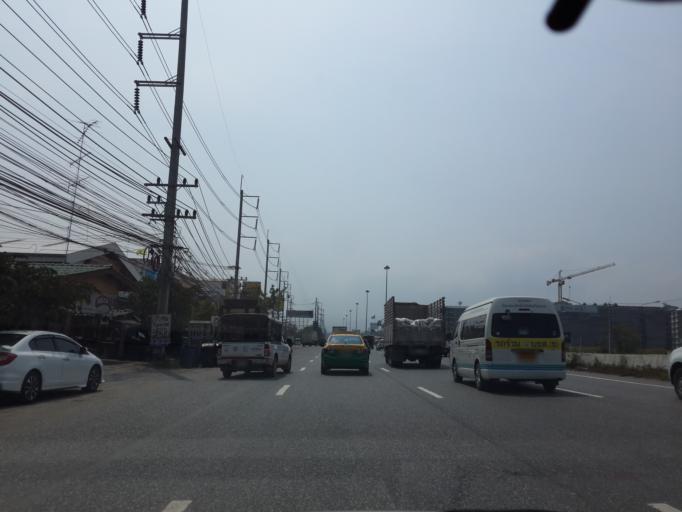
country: TH
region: Chon Buri
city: Chon Buri
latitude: 13.4185
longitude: 100.9977
